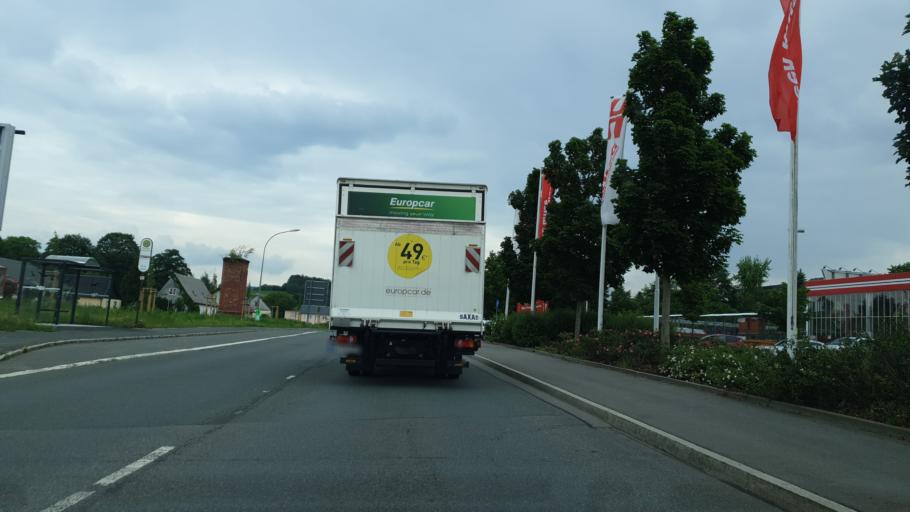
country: DE
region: Saxony
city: Rodewisch
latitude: 50.5409
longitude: 12.3957
